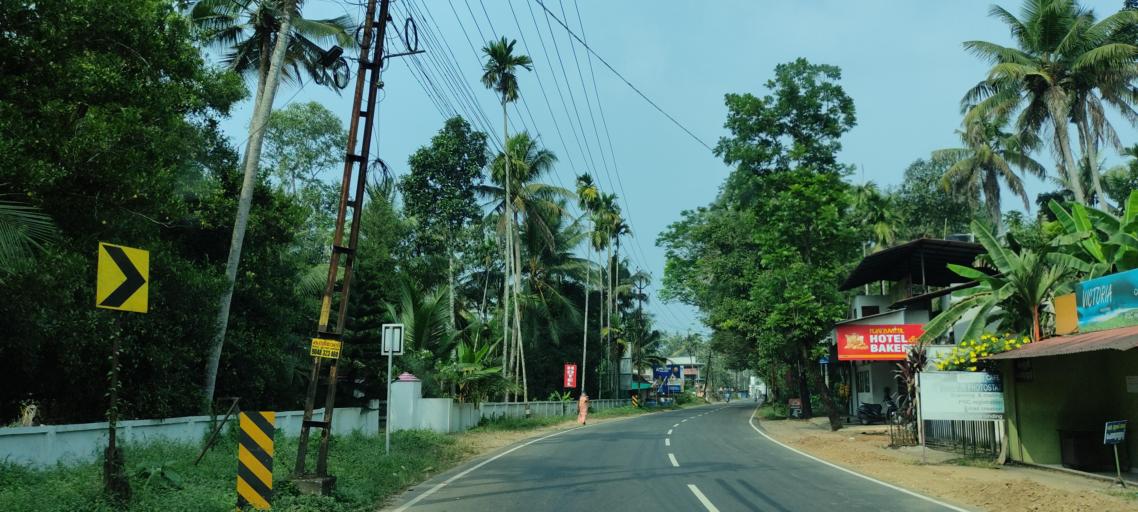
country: IN
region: Kerala
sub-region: Kottayam
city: Vaikam
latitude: 9.7646
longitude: 76.4147
